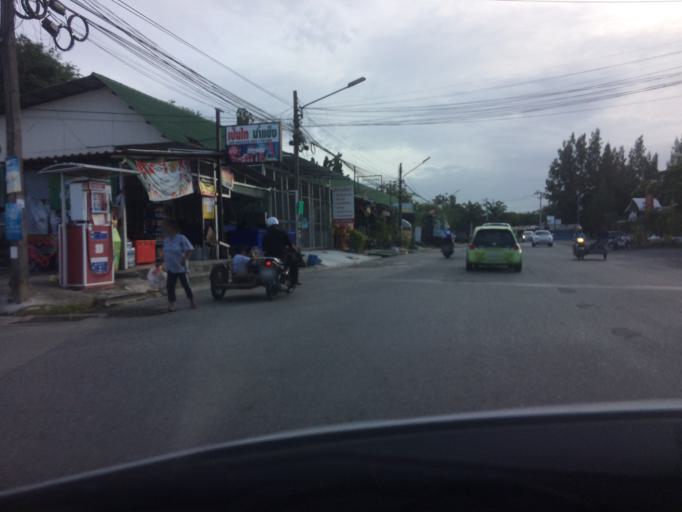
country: TH
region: Phuket
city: Ban Talat Yai
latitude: 7.8754
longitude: 98.3980
